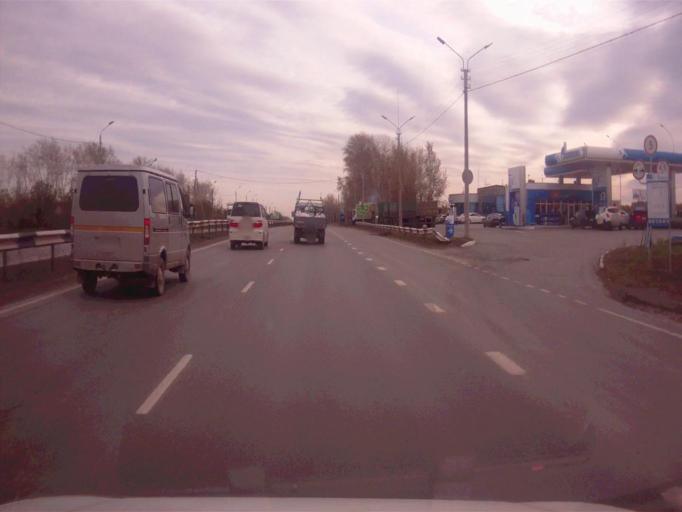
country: RU
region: Chelyabinsk
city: Novosineglazovskiy
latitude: 55.0556
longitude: 61.4073
